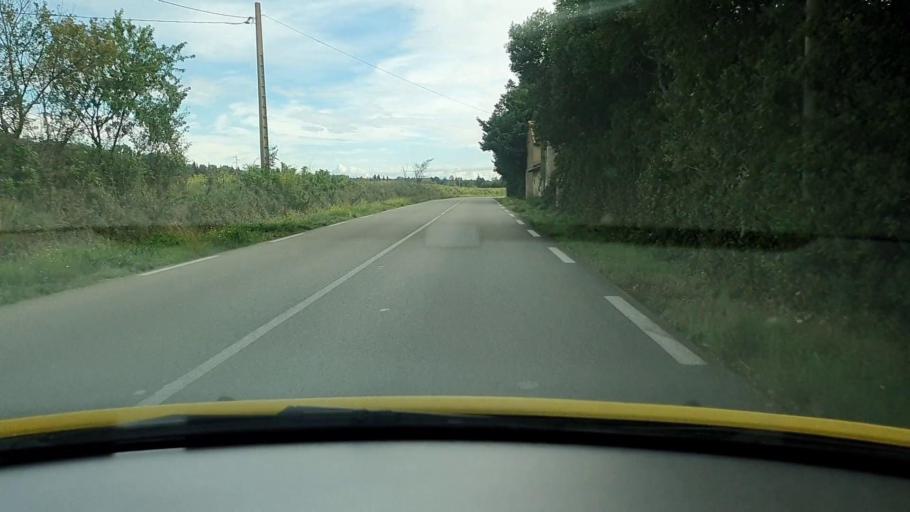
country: FR
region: Languedoc-Roussillon
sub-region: Departement du Gard
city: Bellegarde
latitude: 43.7779
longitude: 4.5442
